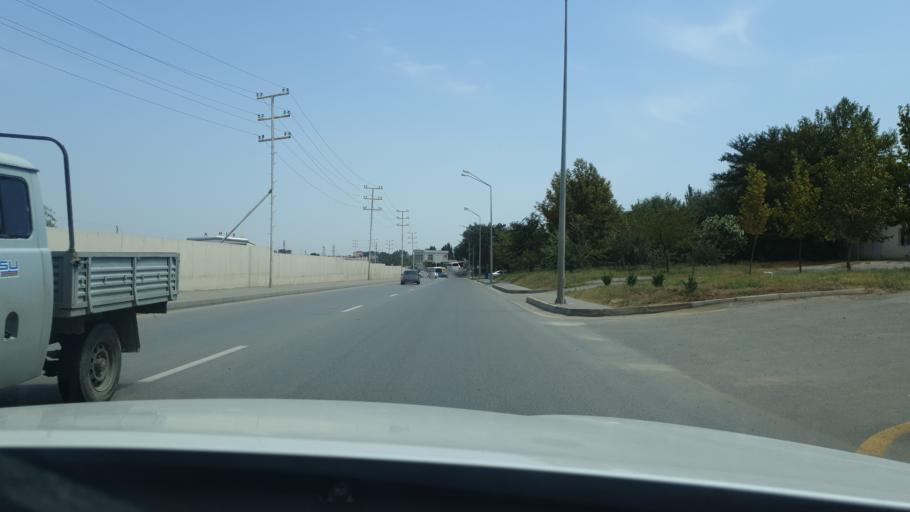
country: AZ
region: Baki
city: Qaracuxur
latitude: 40.3928
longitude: 49.9788
